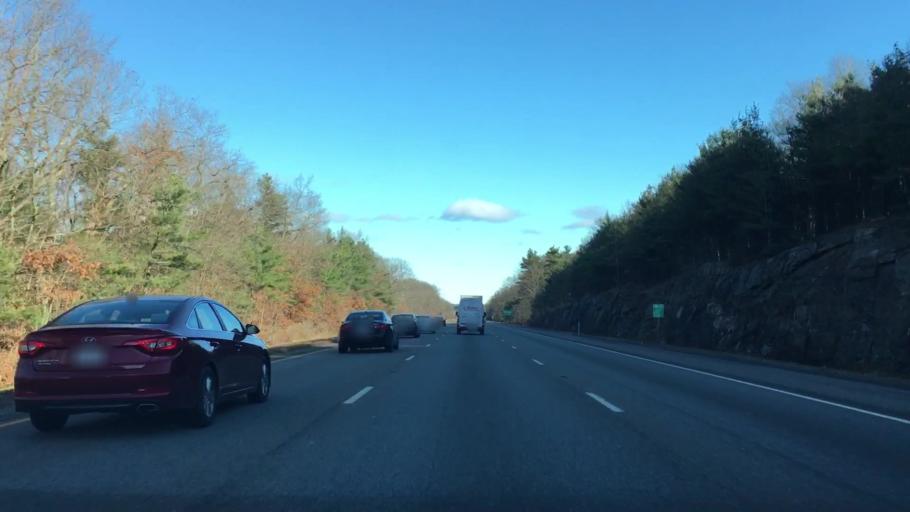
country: US
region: Massachusetts
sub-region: Worcester County
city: Bolton
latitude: 42.4212
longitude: -71.6006
